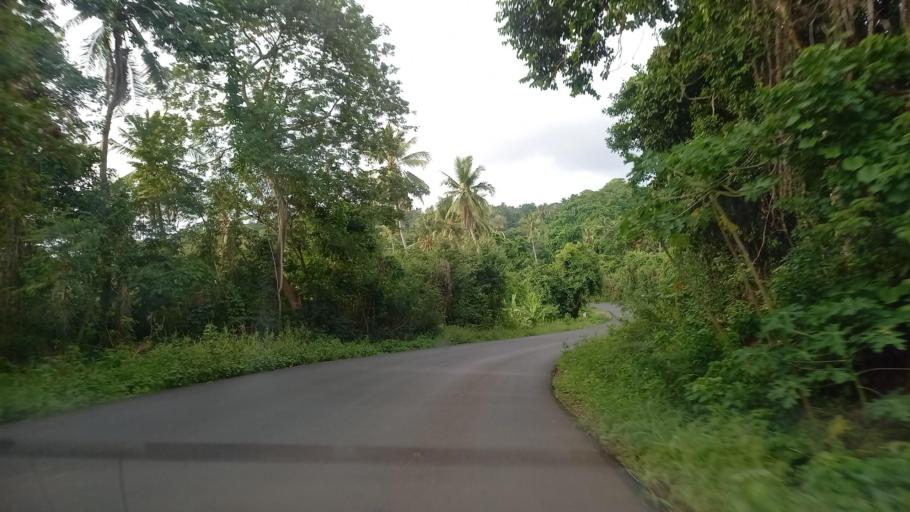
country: YT
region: M'Tsangamouji
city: M'Tsangamouji
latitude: -12.7519
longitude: 45.0644
